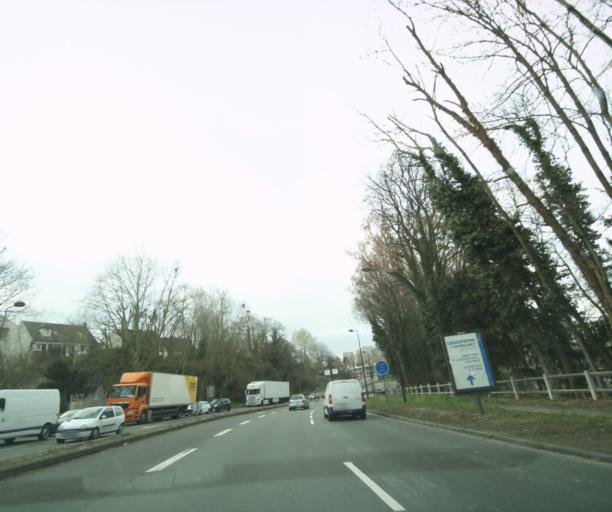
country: FR
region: Ile-de-France
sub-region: Departement des Yvelines
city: Louveciennes
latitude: 48.8731
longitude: 2.1019
